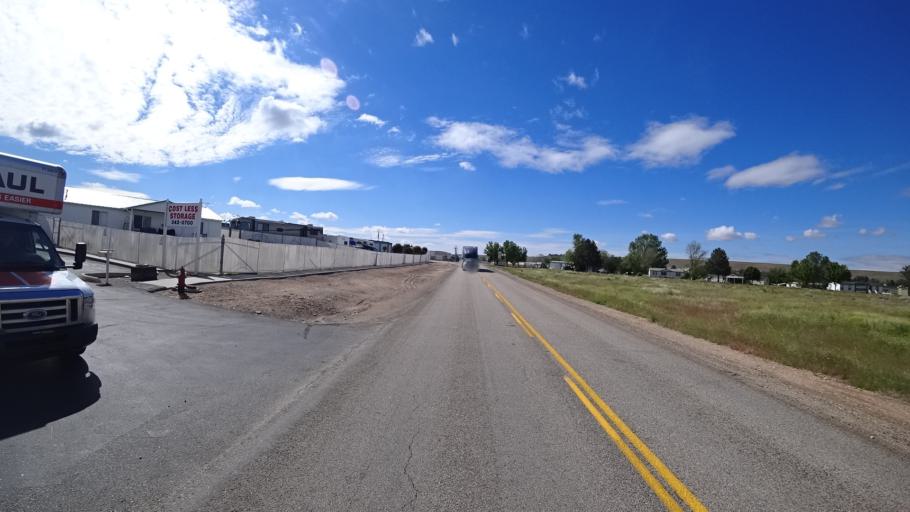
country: US
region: Idaho
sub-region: Ada County
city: Boise
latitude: 43.5289
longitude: -116.1564
